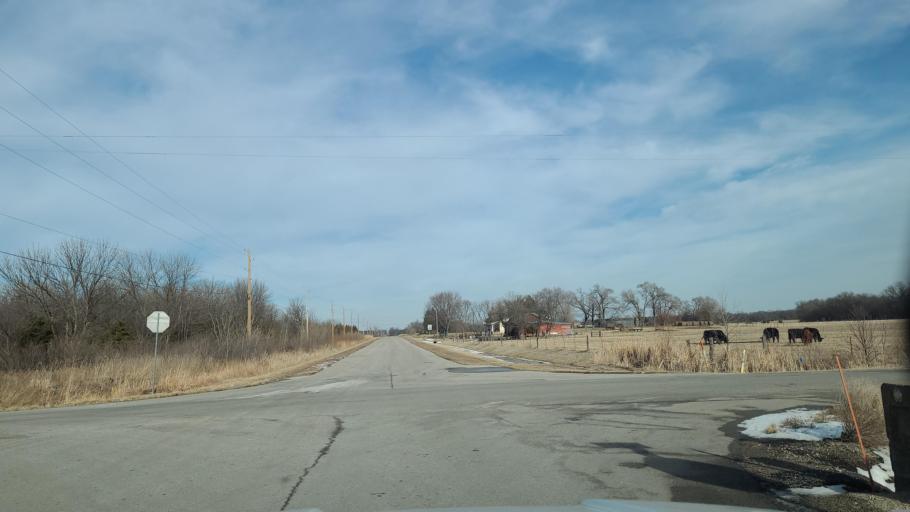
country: US
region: Kansas
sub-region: Douglas County
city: Lawrence
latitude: 38.8988
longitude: -95.2052
